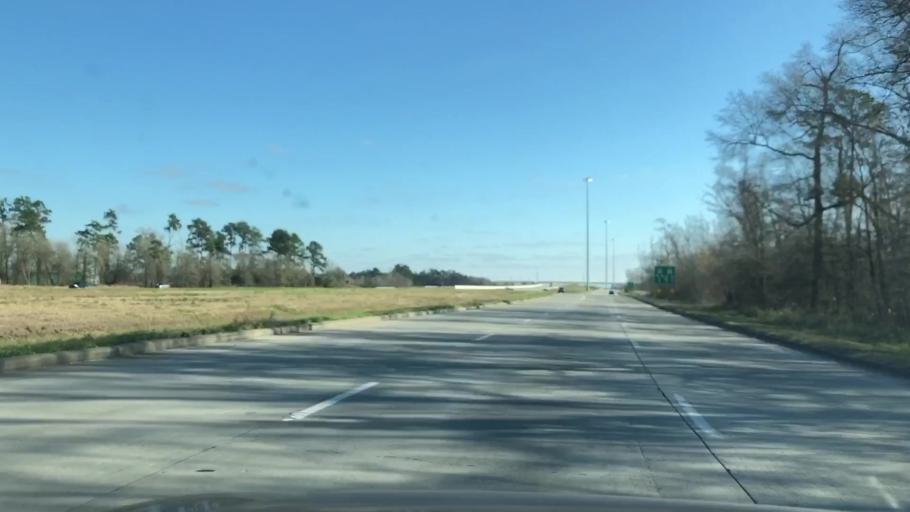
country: US
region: Texas
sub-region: Harris County
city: Cloverleaf
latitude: 29.8251
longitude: -95.1915
